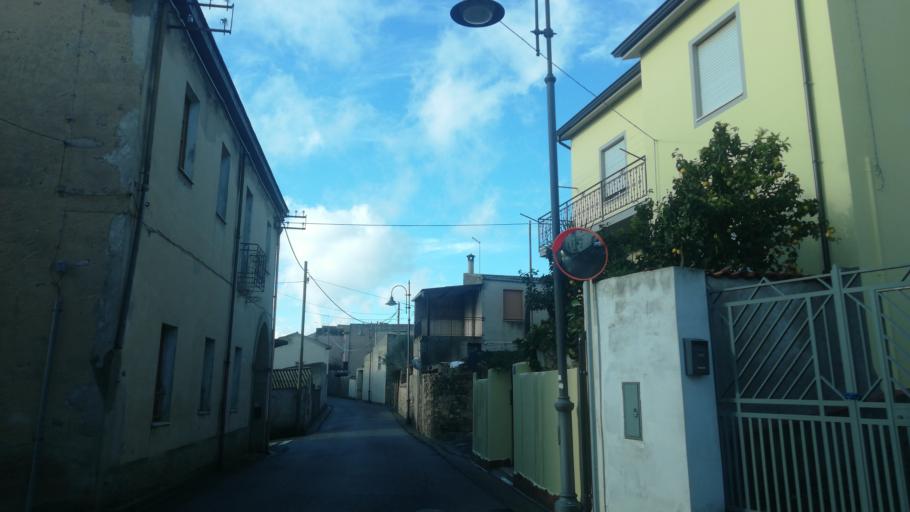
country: IT
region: Sardinia
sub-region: Provincia di Medio Campidano
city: Villanovaforru
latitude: 39.6320
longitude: 8.8708
